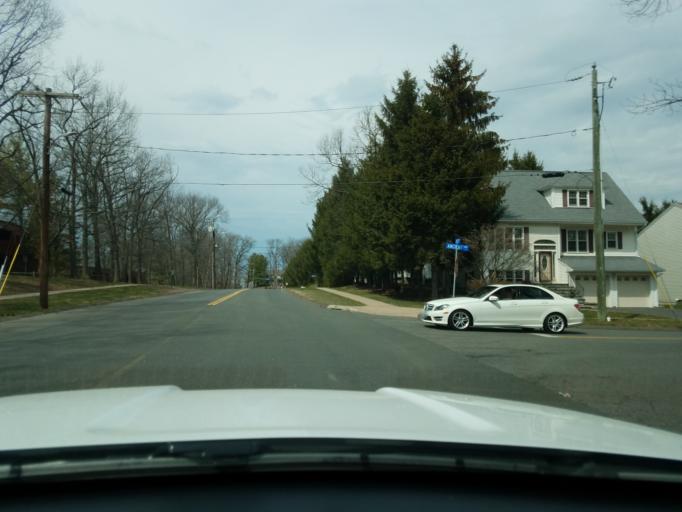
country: US
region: Connecticut
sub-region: Hartford County
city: Newington
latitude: 41.6739
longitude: -72.7086
